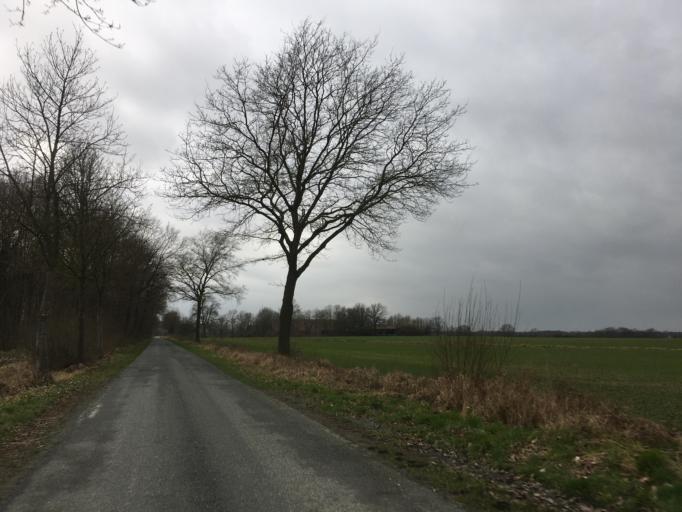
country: DE
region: North Rhine-Westphalia
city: Ludinghausen
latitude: 51.8057
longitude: 7.4679
